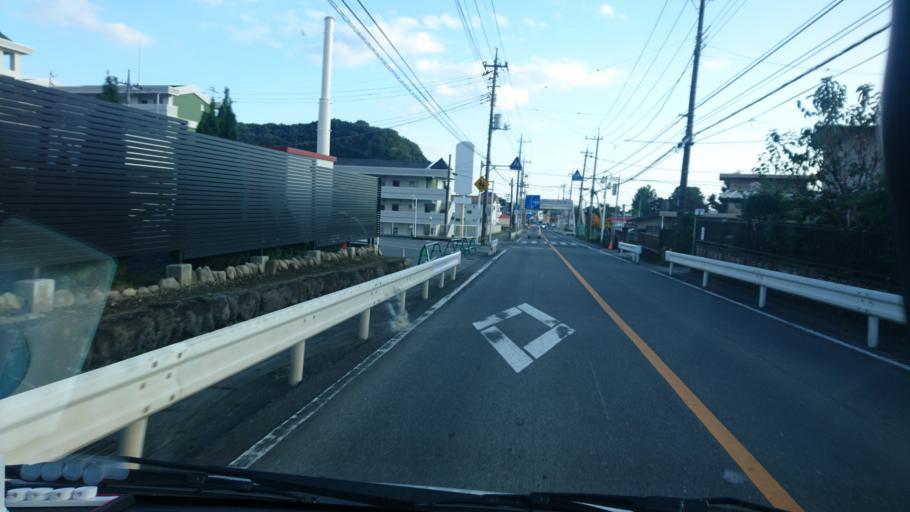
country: JP
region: Gunma
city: Omamacho-omama
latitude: 36.4431
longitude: 139.2767
